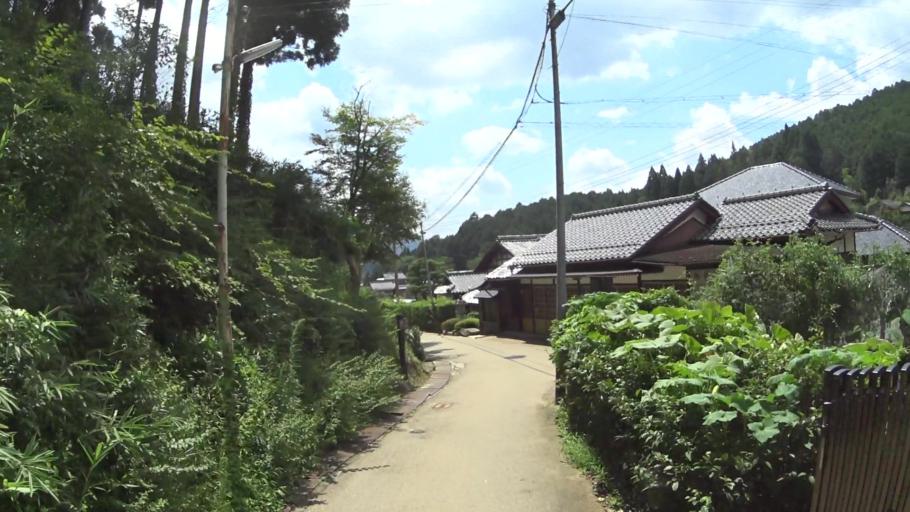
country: JP
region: Shiga Prefecture
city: Kitahama
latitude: 35.1216
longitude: 135.8254
